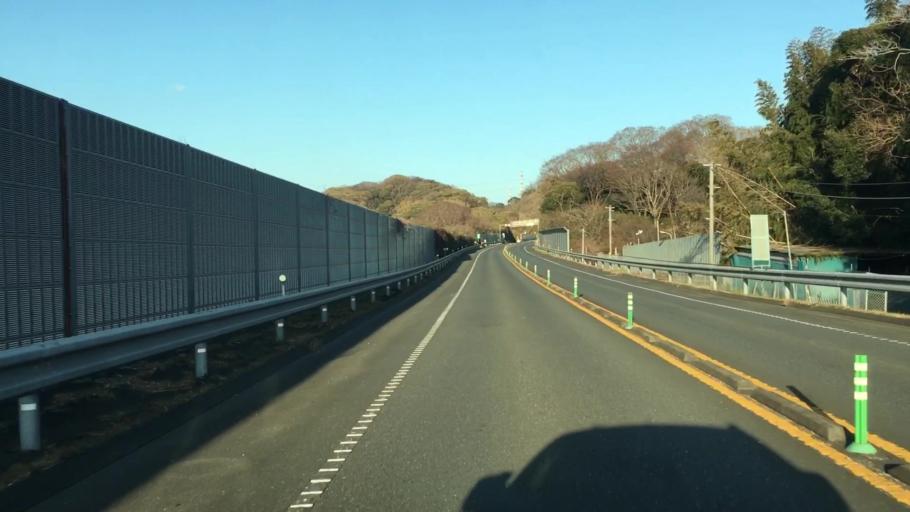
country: JP
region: Kanagawa
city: Yokosuka
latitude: 35.2289
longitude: 139.6435
